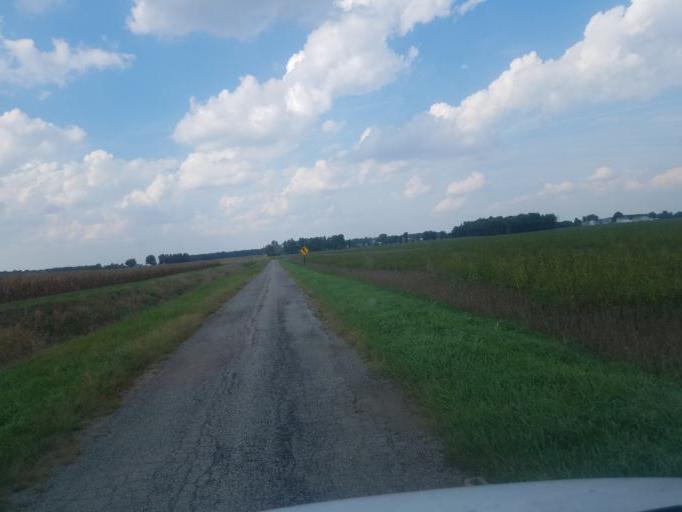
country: US
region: Ohio
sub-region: Hancock County
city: Arlington
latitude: 40.8030
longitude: -83.6897
